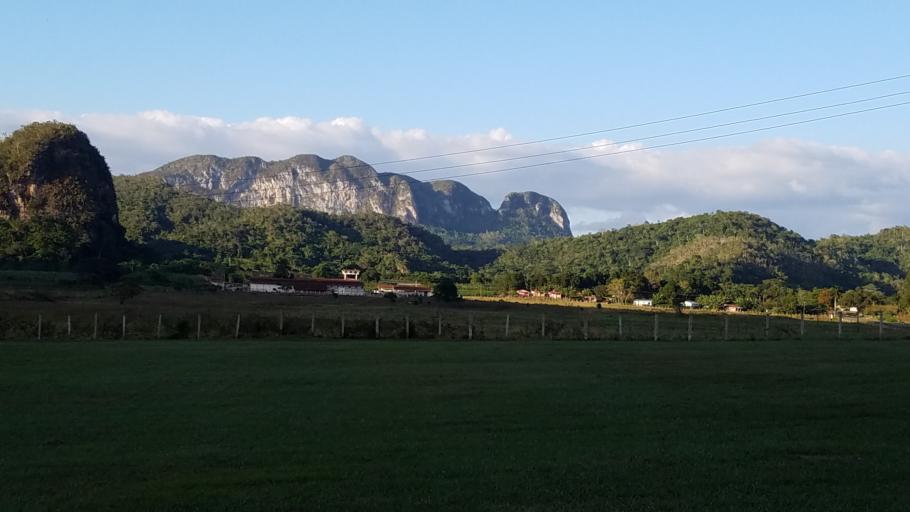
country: CU
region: Pinar del Rio
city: Vinales
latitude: 22.6540
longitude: -83.7157
